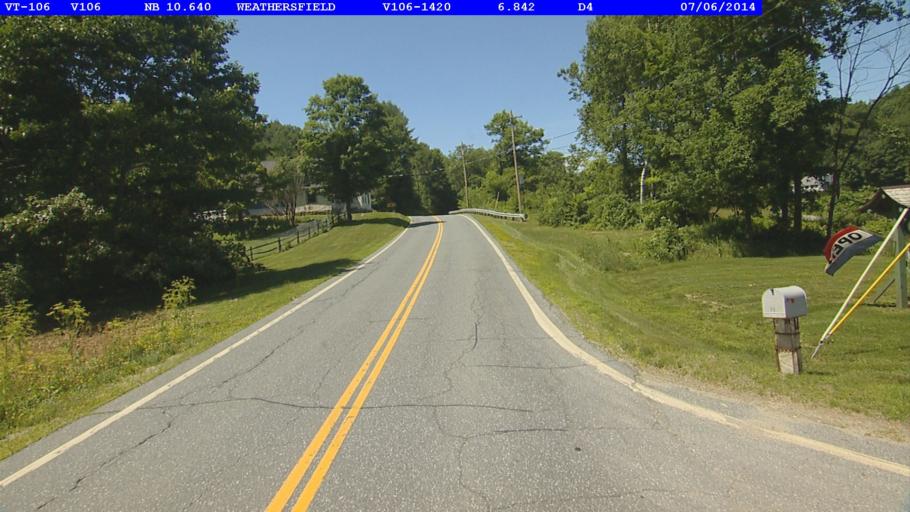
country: US
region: Vermont
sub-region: Windsor County
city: Springfield
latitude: 43.4335
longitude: -72.5279
